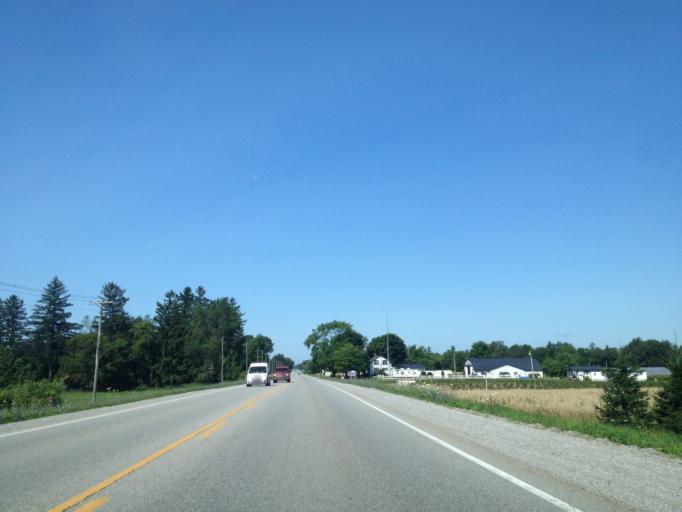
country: CA
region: Ontario
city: Norfolk County
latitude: 42.8336
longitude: -80.3776
